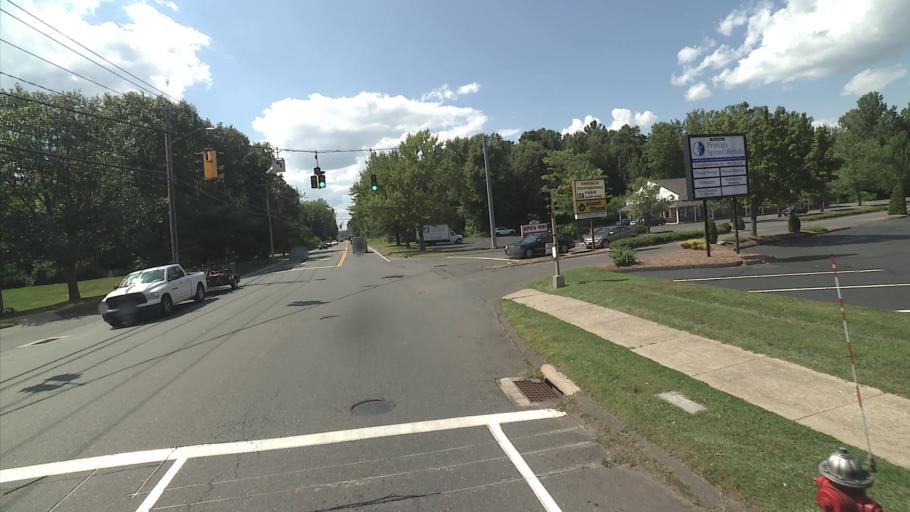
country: US
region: Connecticut
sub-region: Hartford County
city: Hazardville
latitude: 41.9880
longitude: -72.5597
